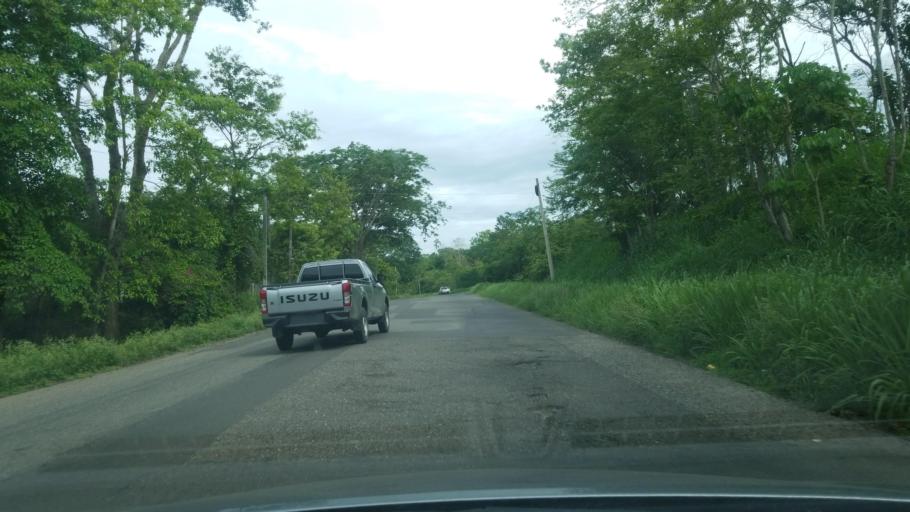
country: HN
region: Santa Barbara
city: Camalote
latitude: 15.3292
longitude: -88.3304
